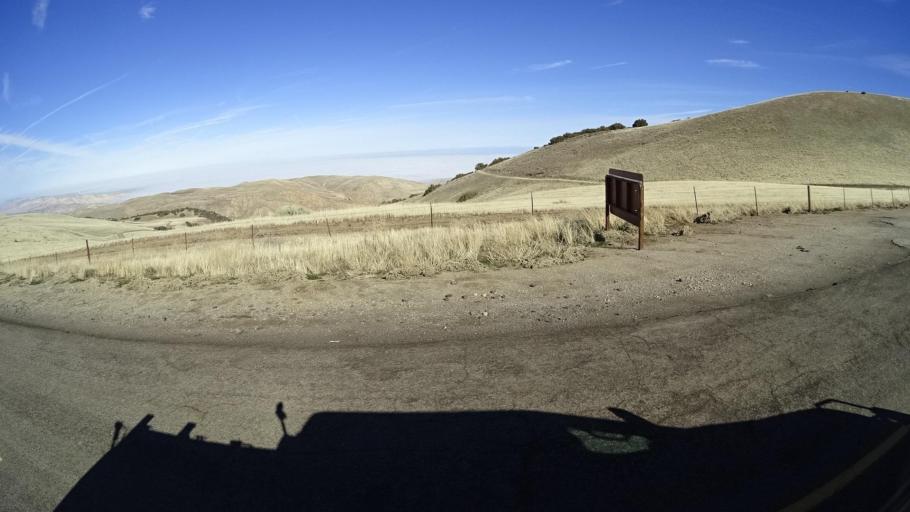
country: US
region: California
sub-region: Kern County
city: Maricopa
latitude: 34.9042
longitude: -119.3771
